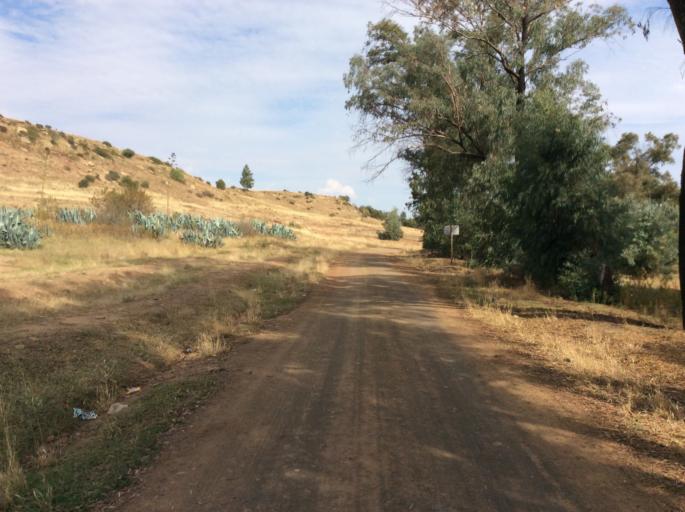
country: ZA
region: Orange Free State
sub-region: Xhariep District Municipality
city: Dewetsdorp
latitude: -29.5862
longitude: 26.6674
